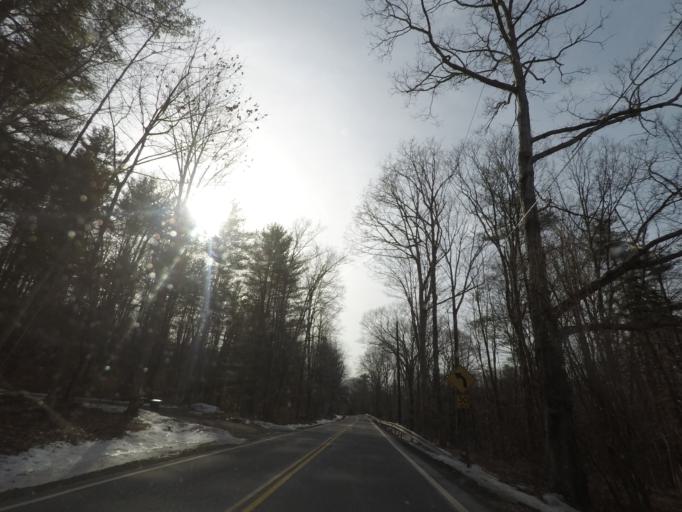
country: US
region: New York
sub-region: Rensselaer County
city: Nassau
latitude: 42.4901
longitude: -73.5549
